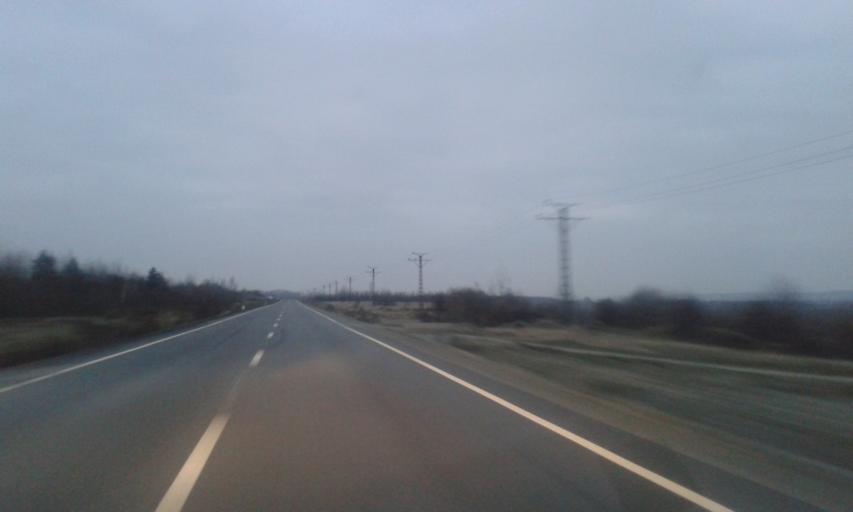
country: RO
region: Gorj
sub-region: Comuna Bumbesti-Jiu
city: Bumbesti-Jiu
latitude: 45.1457
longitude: 23.3703
